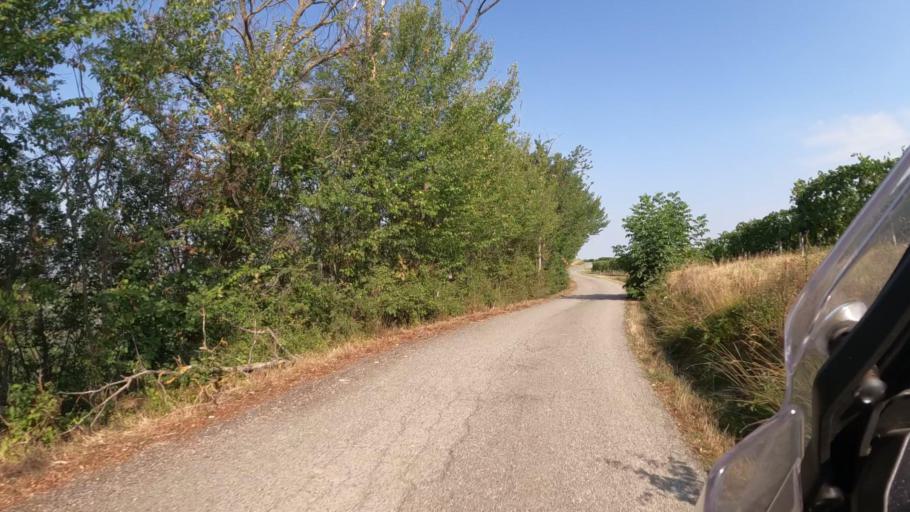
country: IT
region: Piedmont
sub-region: Provincia di Asti
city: Castel Boglione
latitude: 44.7496
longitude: 8.3863
